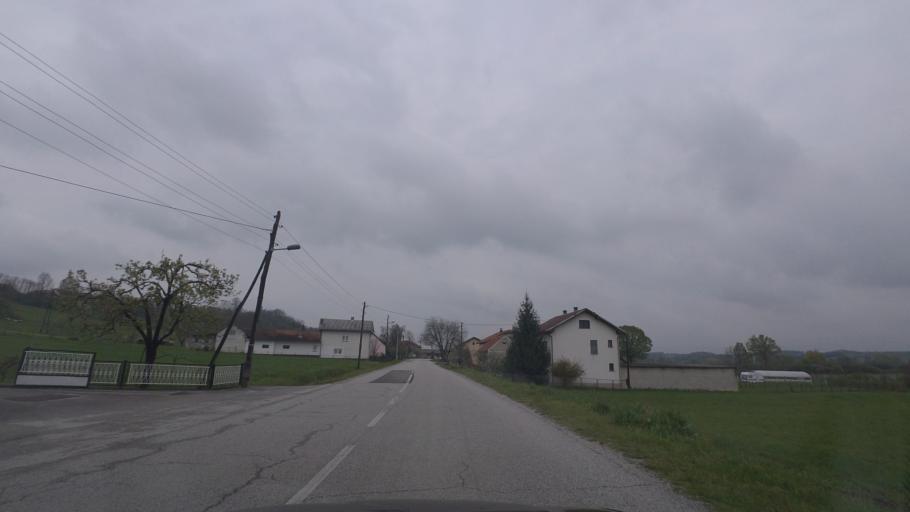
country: HR
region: Zagrebacka
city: Jastrebarsko
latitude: 45.6151
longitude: 15.5823
